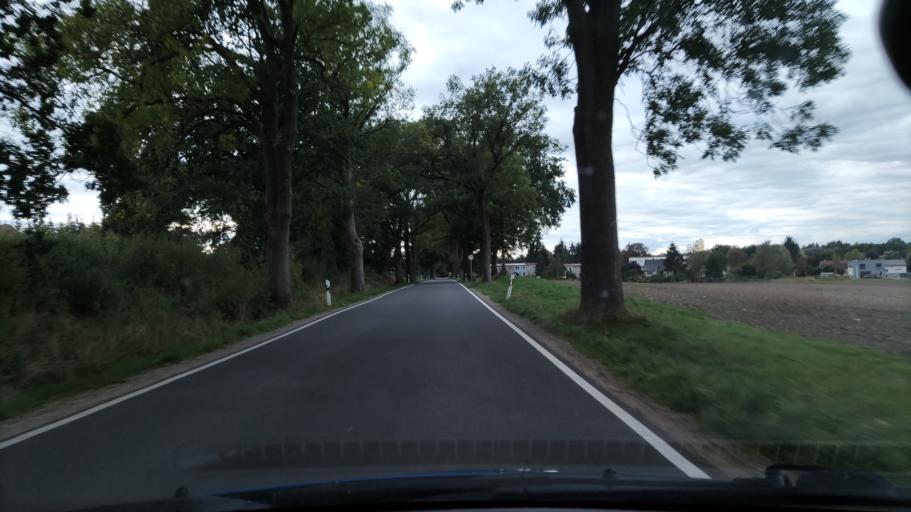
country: DE
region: Mecklenburg-Vorpommern
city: Zarrentin
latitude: 53.4622
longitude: 10.9749
